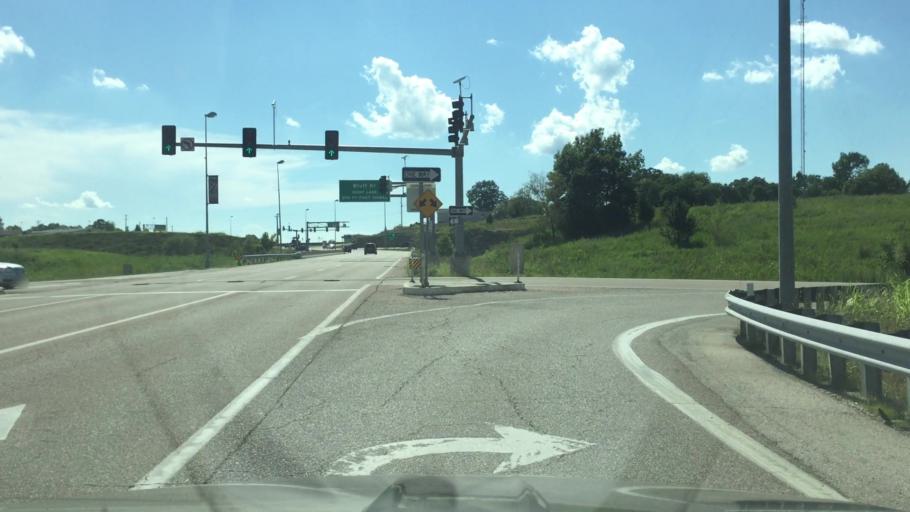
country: US
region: Missouri
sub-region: Camden County
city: Osage Beach
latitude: 38.1560
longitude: -92.6103
